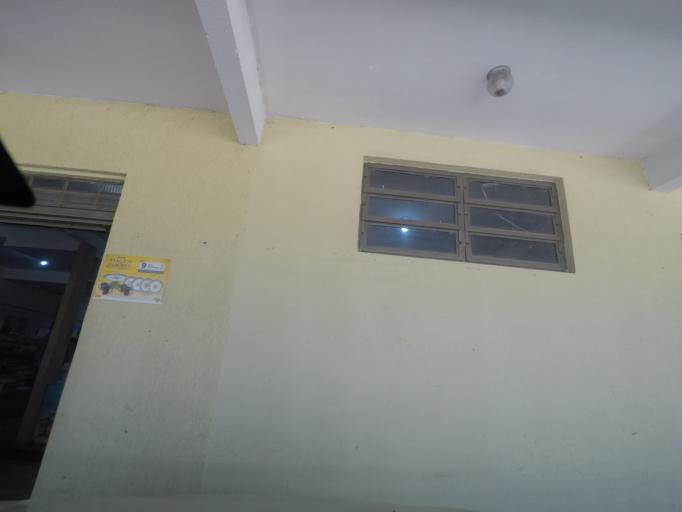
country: BR
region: Goias
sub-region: Aparecida De Goiania
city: Aparecida de Goiania
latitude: -16.7683
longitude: -49.3480
